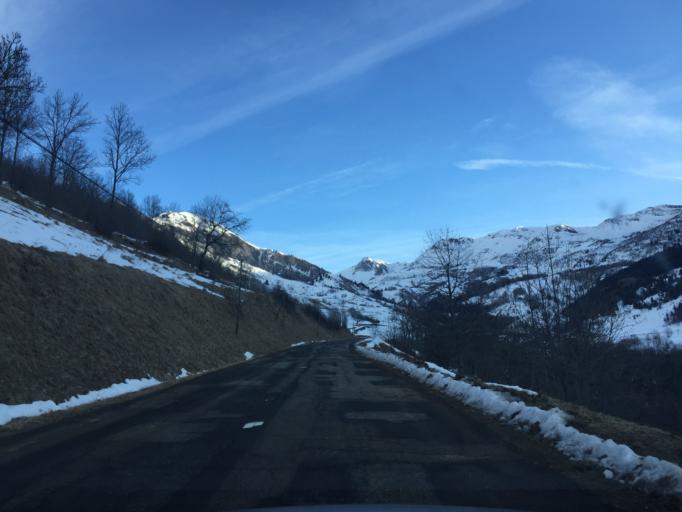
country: FR
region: Rhone-Alpes
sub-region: Departement de la Savoie
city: Aigueblanche
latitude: 45.5564
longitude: 6.5114
